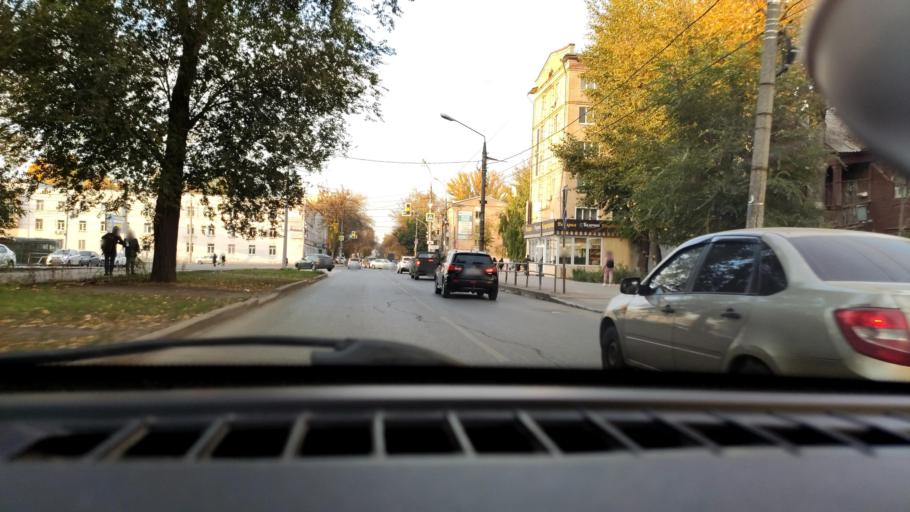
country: RU
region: Samara
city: Samara
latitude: 53.1990
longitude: 50.1785
